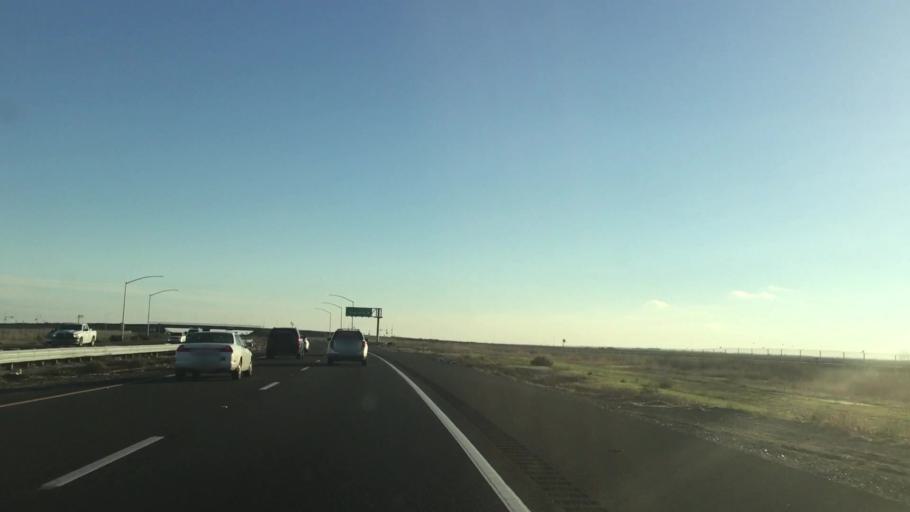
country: US
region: California
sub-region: Sacramento County
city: Elverta
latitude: 38.7582
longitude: -121.5437
